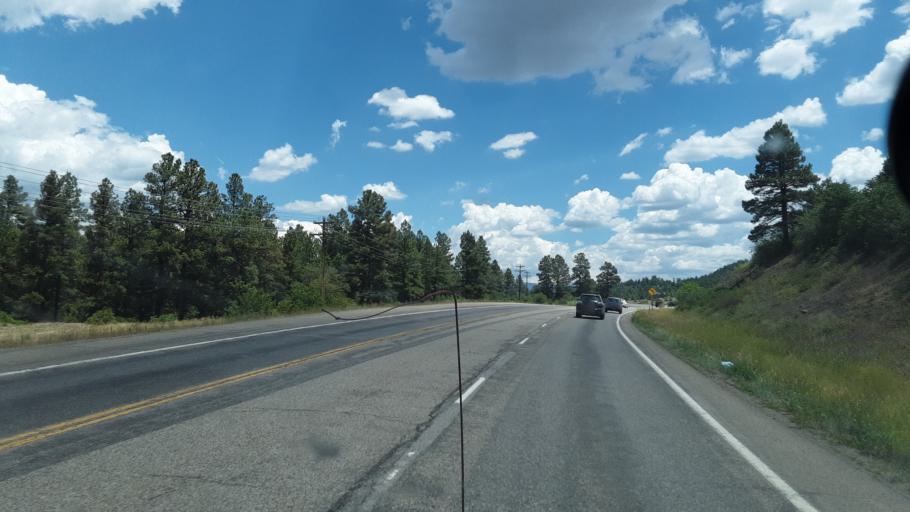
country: US
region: Colorado
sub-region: Archuleta County
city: Pagosa Springs
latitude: 37.2284
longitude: -107.1130
